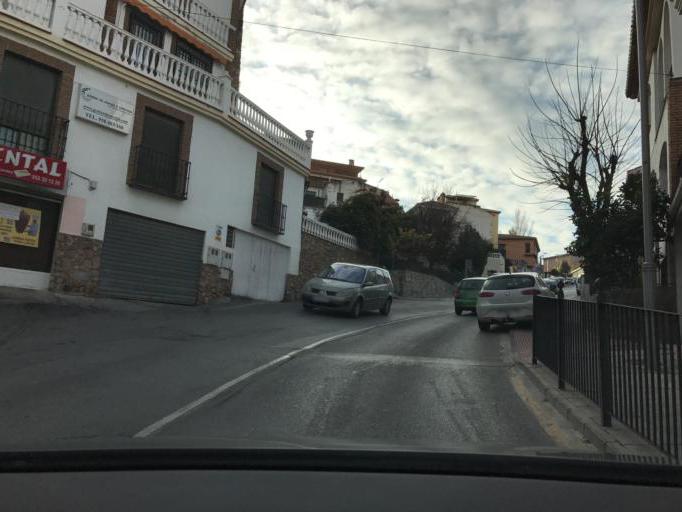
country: ES
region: Andalusia
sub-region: Provincia de Granada
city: Cajar
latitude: 37.1347
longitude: -3.5583
